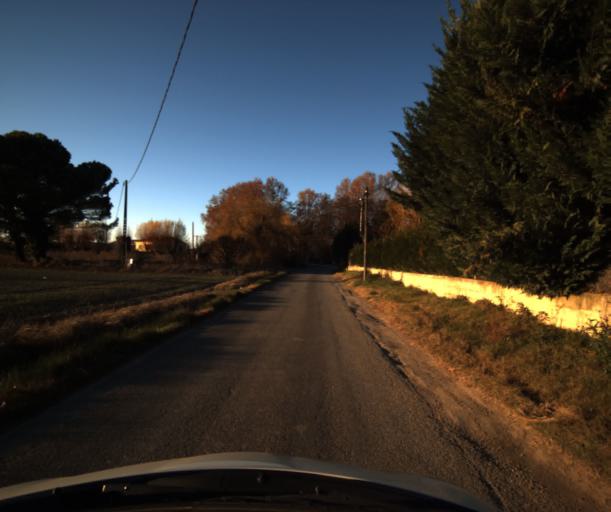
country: FR
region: Provence-Alpes-Cote d'Azur
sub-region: Departement du Vaucluse
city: Pertuis
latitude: 43.6809
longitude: 5.5092
